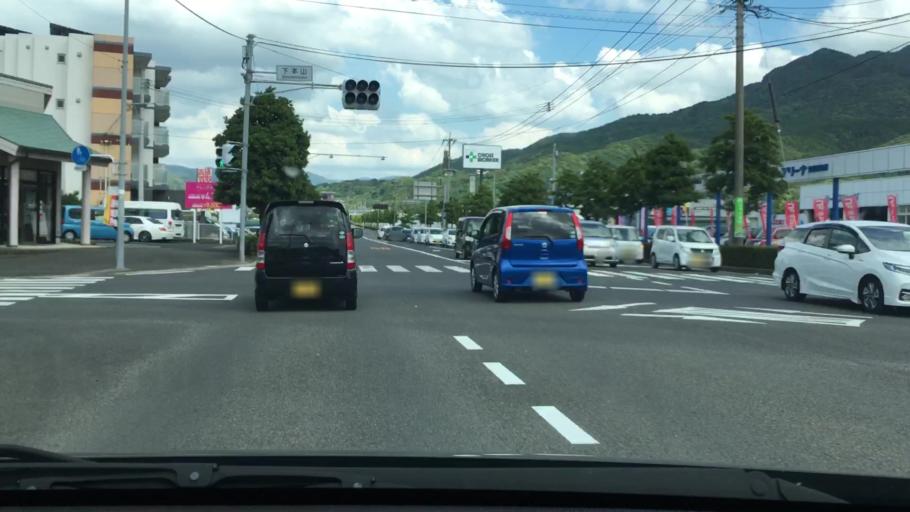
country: JP
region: Nagasaki
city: Sasebo
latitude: 33.2055
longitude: 129.6808
